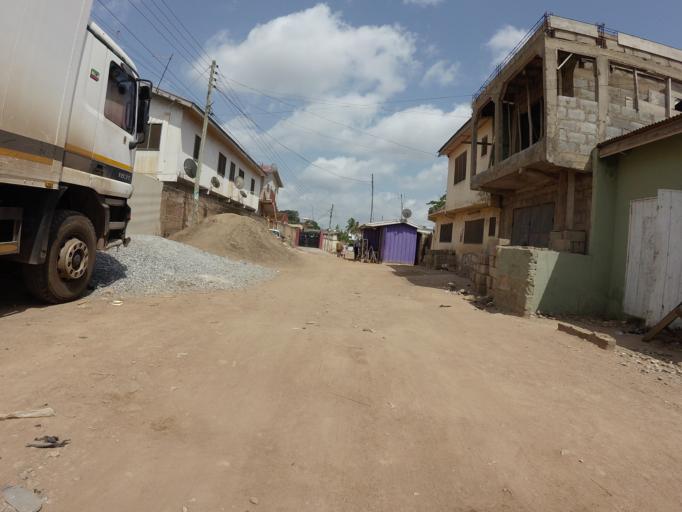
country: GH
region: Greater Accra
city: Dome
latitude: 5.6187
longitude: -0.2488
